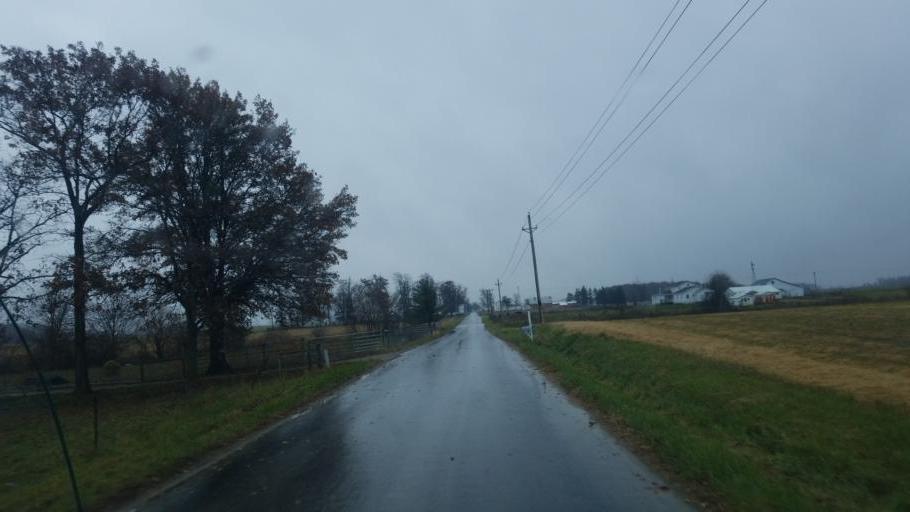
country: US
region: Indiana
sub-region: Adams County
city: Berne
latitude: 40.6466
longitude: -84.8784
